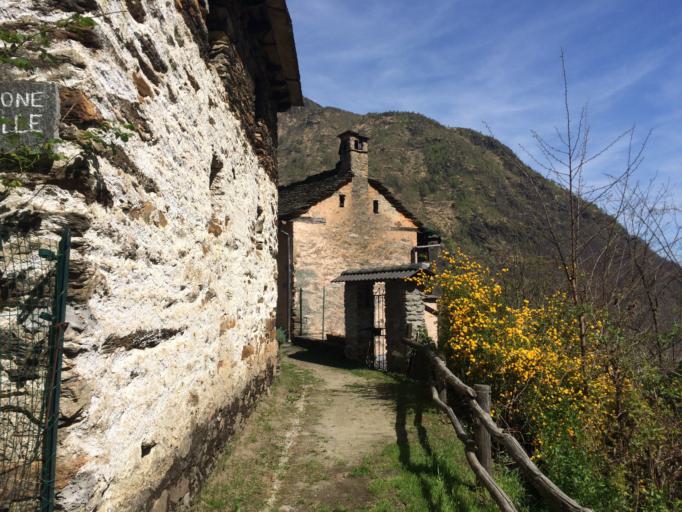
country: IT
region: Piedmont
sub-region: Provincia Verbano-Cusio-Ossola
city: Falmenta
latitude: 46.0795
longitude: 8.5949
